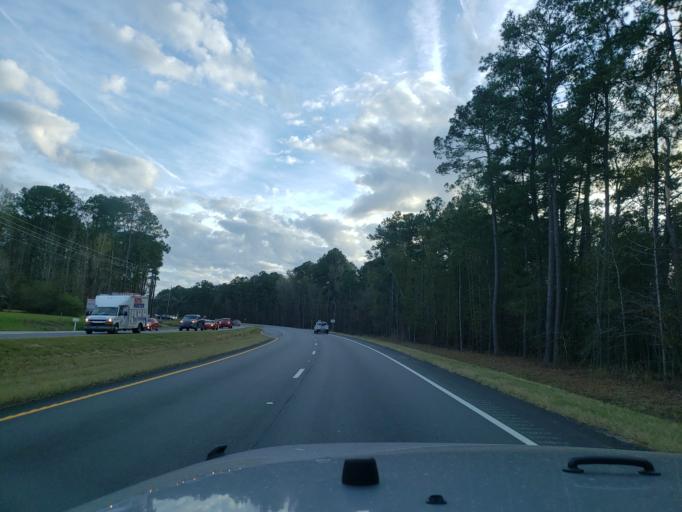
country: US
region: Georgia
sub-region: Chatham County
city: Port Wentworth
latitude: 32.2101
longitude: -81.2011
